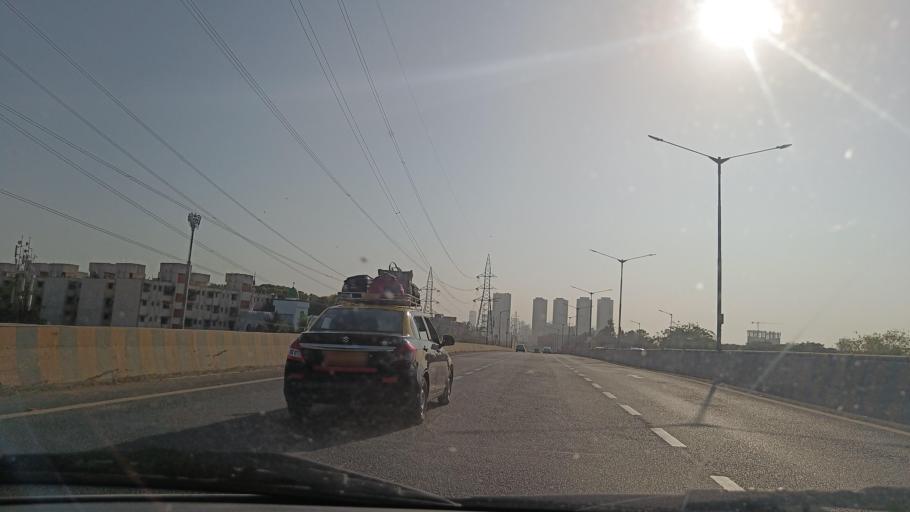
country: IN
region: Maharashtra
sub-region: Mumbai Suburban
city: Mumbai
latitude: 19.0324
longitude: 72.8953
